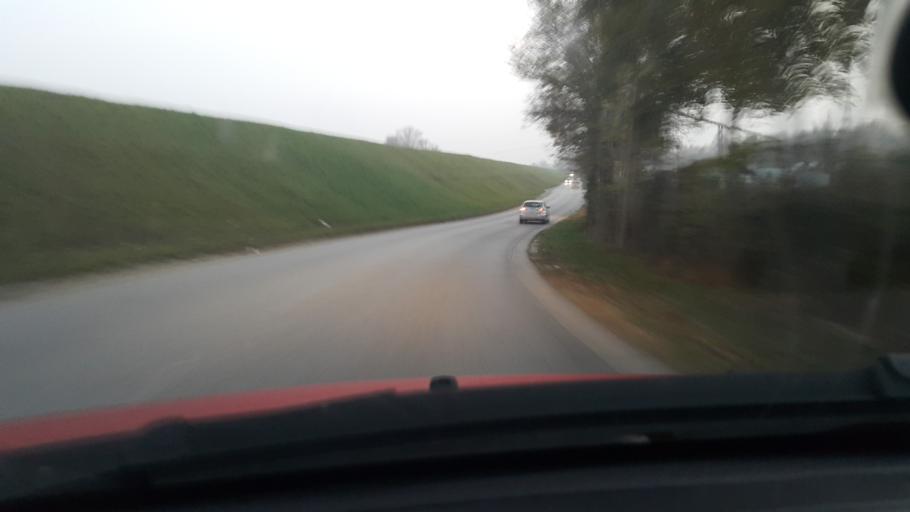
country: SI
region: Miklavz na Dravskem Polju
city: Miklavz na Dravskem Polju
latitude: 46.5252
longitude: 15.7017
